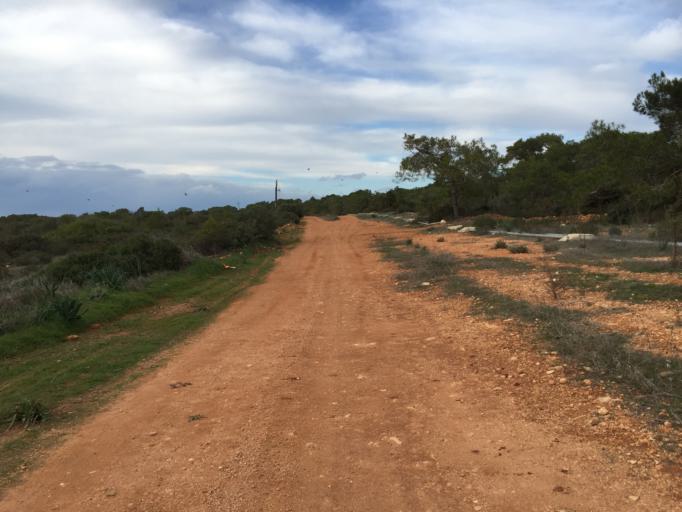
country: CY
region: Pafos
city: Pegeia
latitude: 34.8923
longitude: 32.3730
